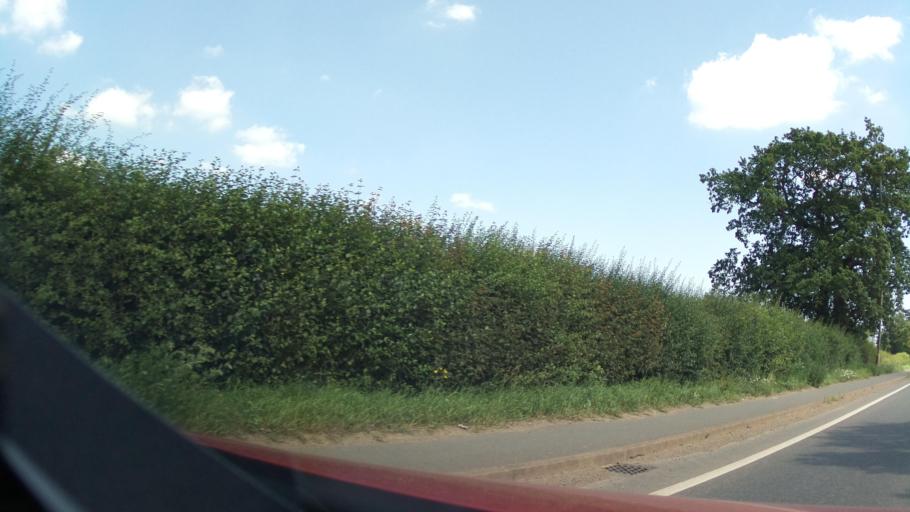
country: GB
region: England
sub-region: Warwickshire
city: Attleborough
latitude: 52.5417
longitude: -1.4332
